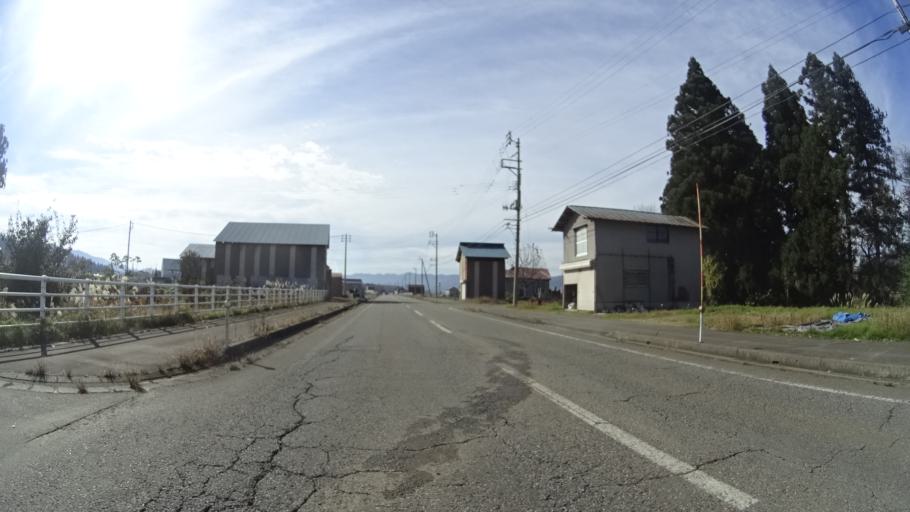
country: JP
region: Niigata
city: Muikamachi
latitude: 37.1795
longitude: 138.9749
